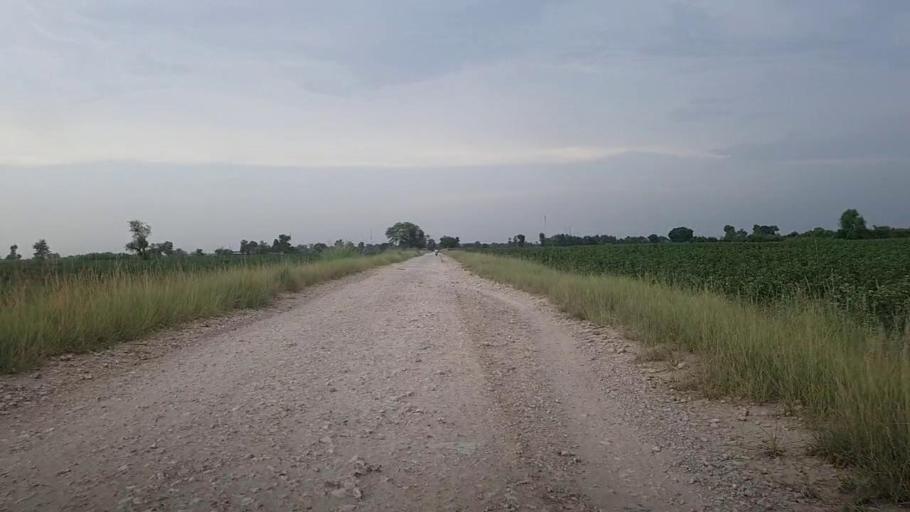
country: PK
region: Sindh
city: Karaundi
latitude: 26.9719
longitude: 68.3438
